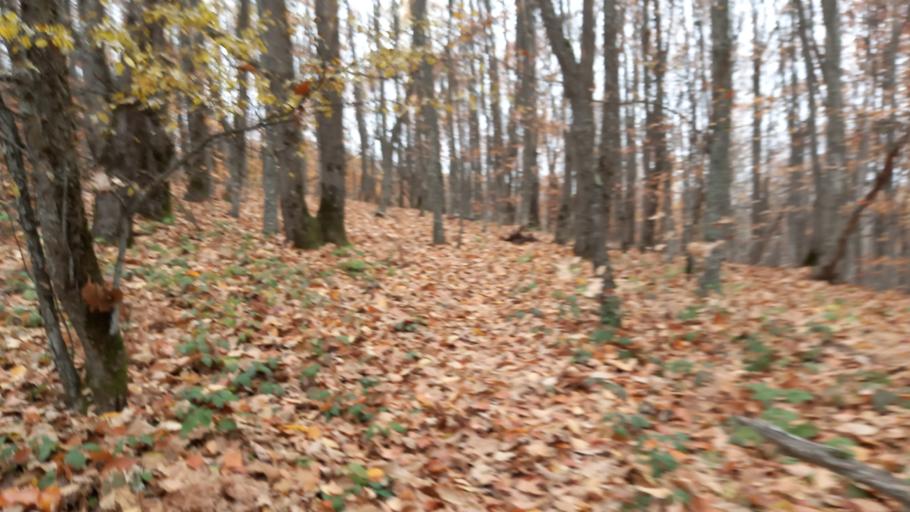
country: RU
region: Krasnodarskiy
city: Goryachiy Klyuch
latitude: 44.4938
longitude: 39.2741
